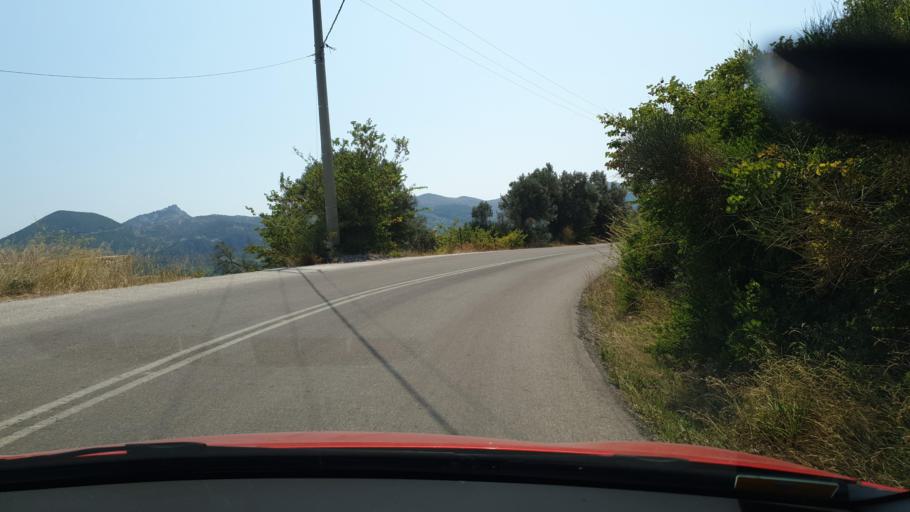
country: GR
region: Central Greece
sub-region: Nomos Evvoias
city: Kymi
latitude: 38.6121
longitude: 24.0796
